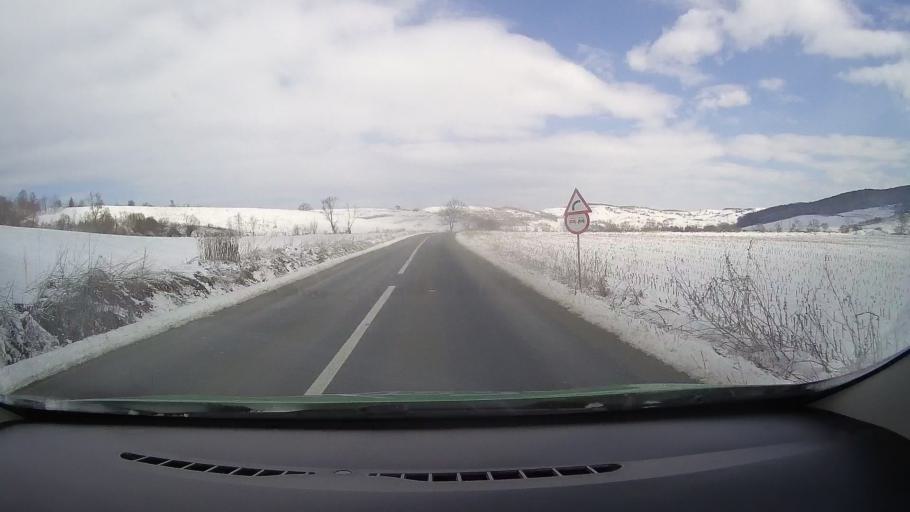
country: RO
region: Sibiu
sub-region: Comuna Altina
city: Altina
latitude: 45.9615
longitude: 24.4595
